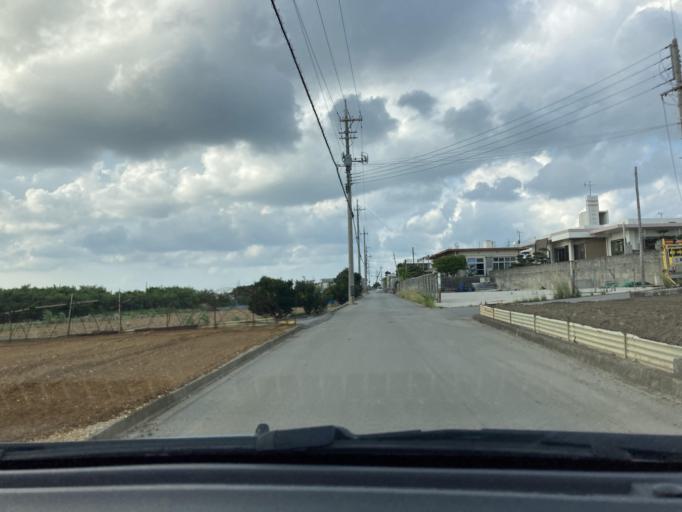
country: JP
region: Okinawa
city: Itoman
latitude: 26.0874
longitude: 127.6620
